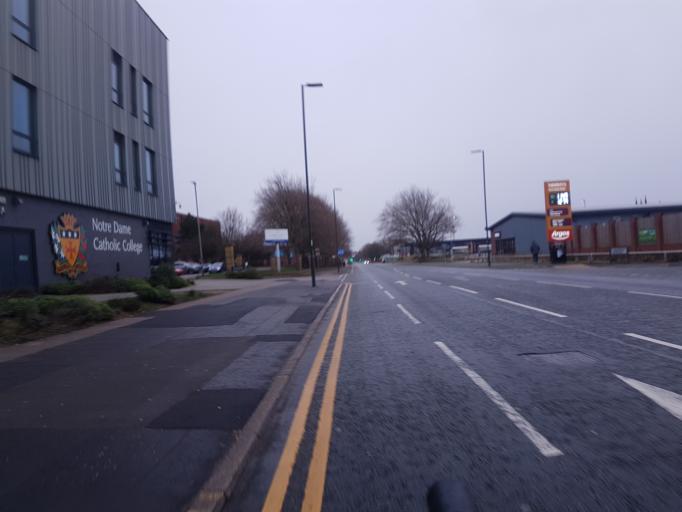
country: GB
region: England
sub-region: Liverpool
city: Liverpool
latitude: 53.4253
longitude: -2.9788
